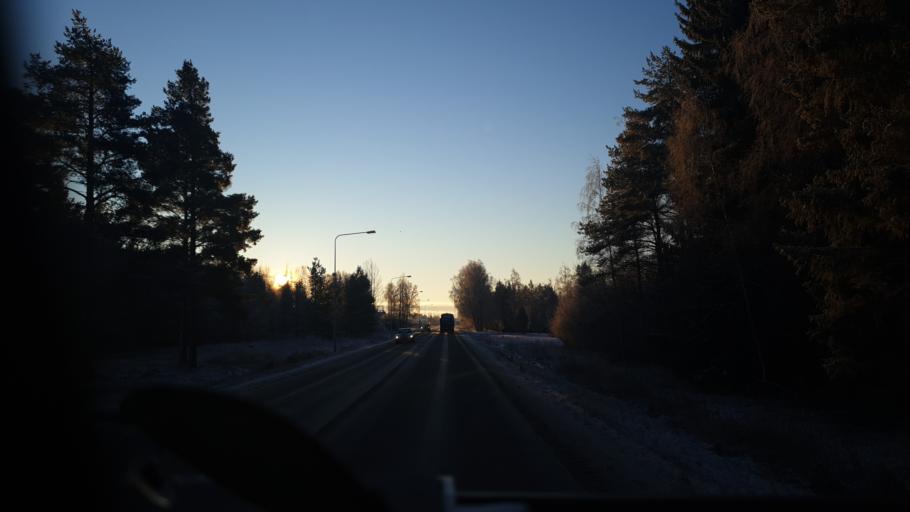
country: FI
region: Northern Ostrobothnia
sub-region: Ylivieska
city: Kalajoki
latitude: 64.2705
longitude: 23.9490
